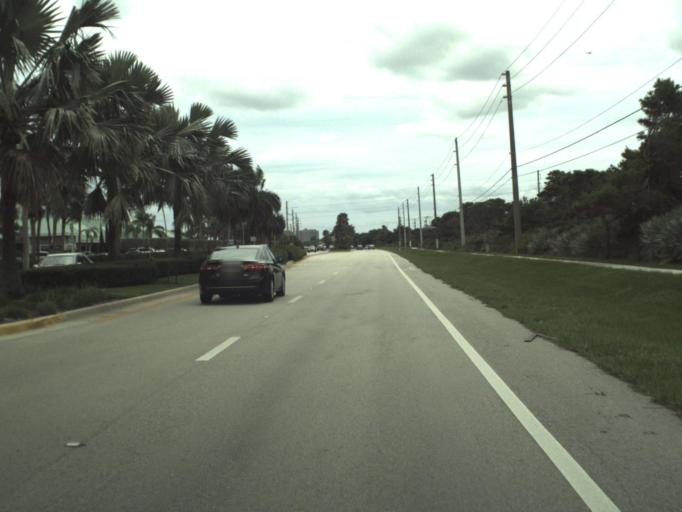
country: US
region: Florida
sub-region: Palm Beach County
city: Jupiter
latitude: 26.9146
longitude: -80.0713
